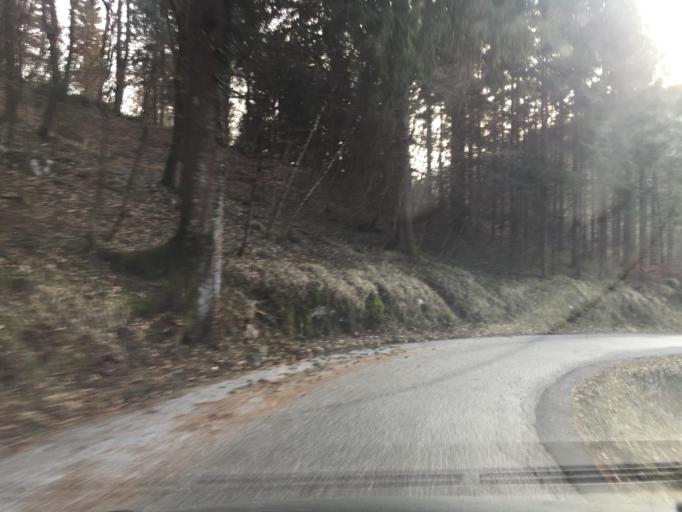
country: SI
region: Kanal
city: Kanal
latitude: 46.0568
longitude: 13.6670
